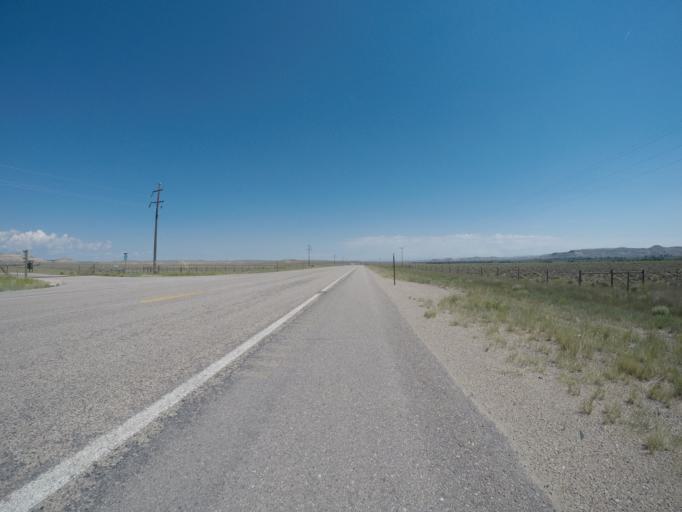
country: US
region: Wyoming
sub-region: Sublette County
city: Marbleton
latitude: 42.4098
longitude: -110.1180
